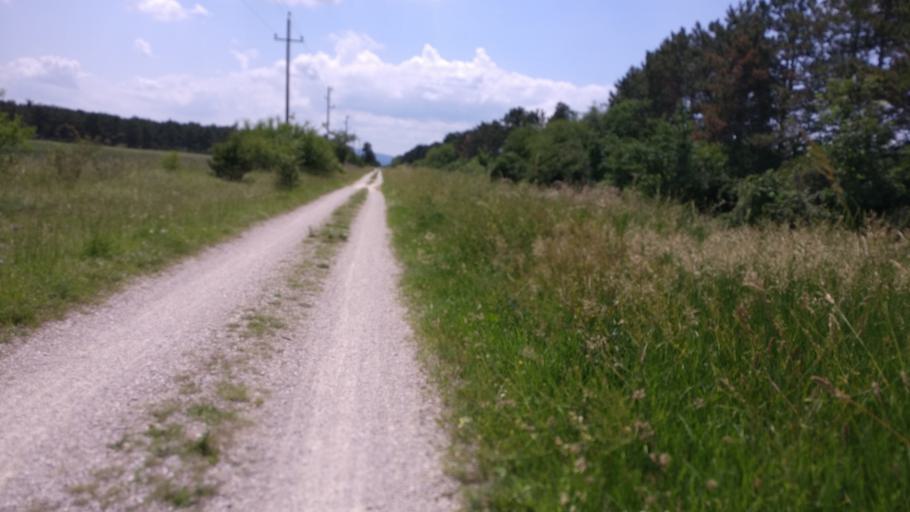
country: AT
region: Lower Austria
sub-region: Politischer Bezirk Wiener Neustadt
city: Lichtenworth
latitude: 47.8672
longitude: 16.2815
